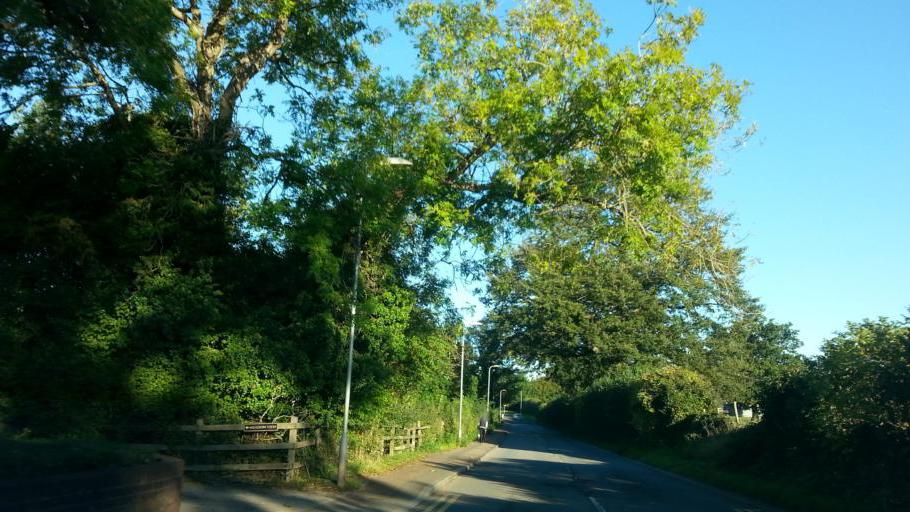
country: GB
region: Wales
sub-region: Monmouthshire
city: Monmouth
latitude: 51.8151
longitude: -2.7277
